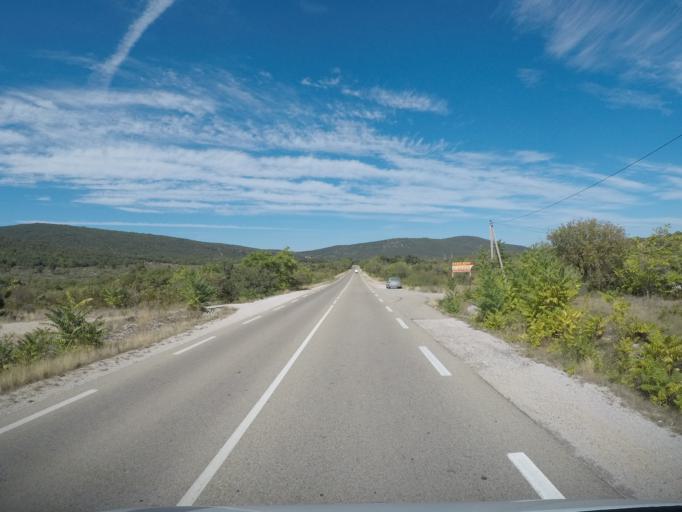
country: FR
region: Languedoc-Roussillon
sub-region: Departement de l'Herault
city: Saint-Martin-de-Londres
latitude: 43.8240
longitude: 3.7446
